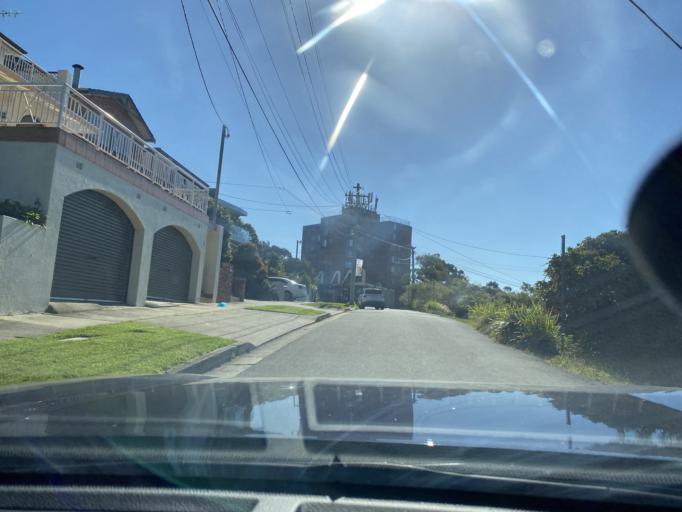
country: AU
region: New South Wales
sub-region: Canada Bay
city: Canada Bay
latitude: -33.8483
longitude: 151.1422
